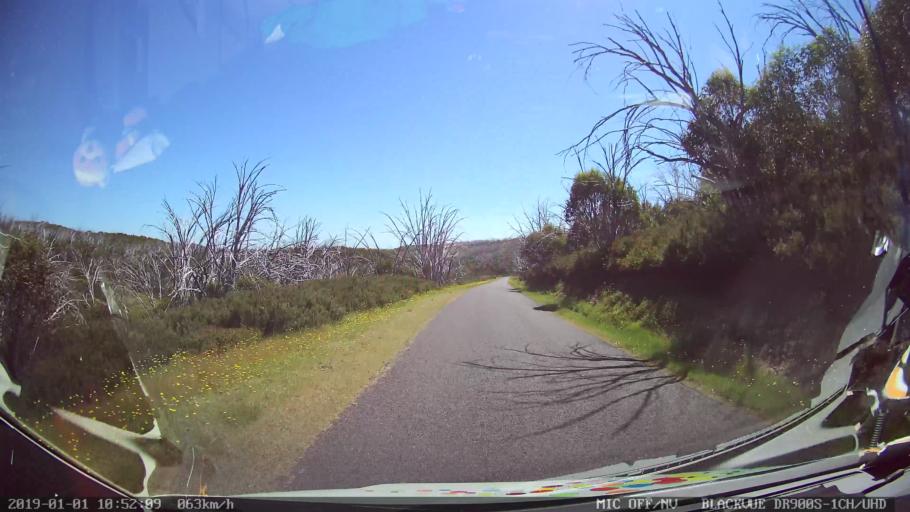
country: AU
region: New South Wales
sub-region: Snowy River
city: Jindabyne
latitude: -36.0173
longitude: 148.3776
